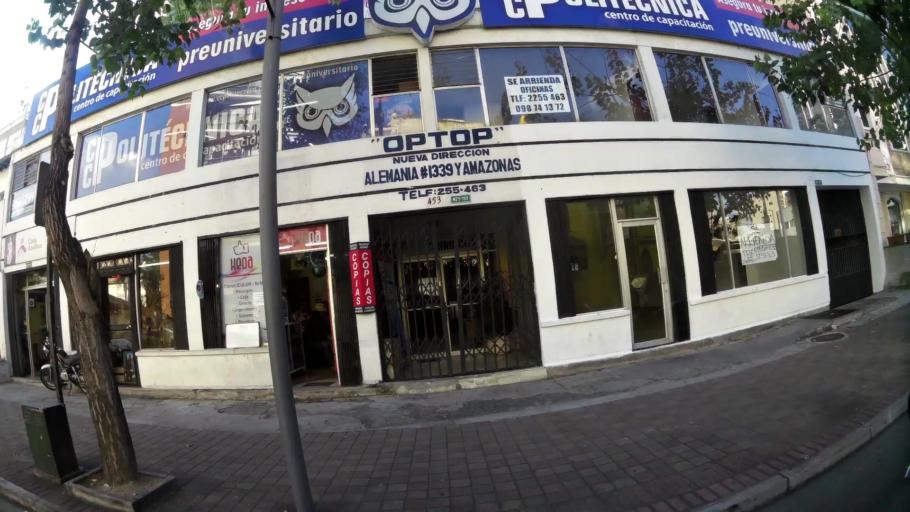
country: EC
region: Pichincha
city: Quito
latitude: -0.2053
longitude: -78.4946
